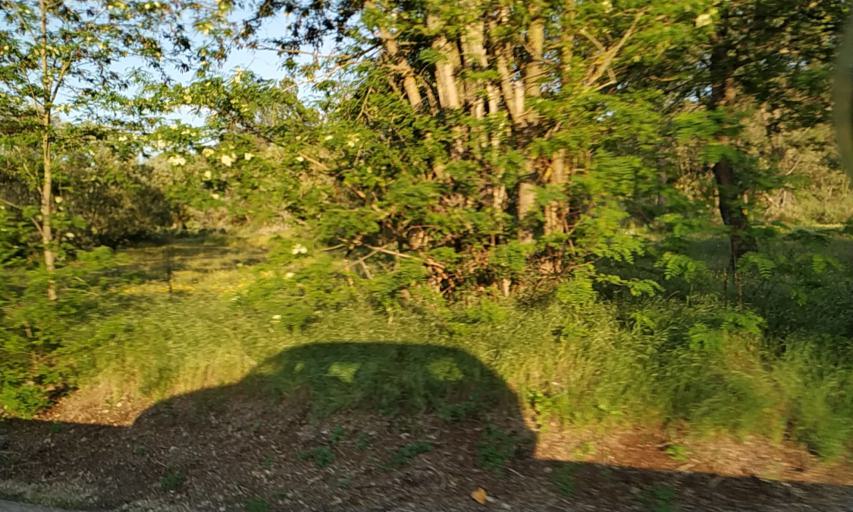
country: ES
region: Extremadura
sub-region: Provincia de Caceres
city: Valencia de Alcantara
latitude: 39.3660
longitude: -7.2708
